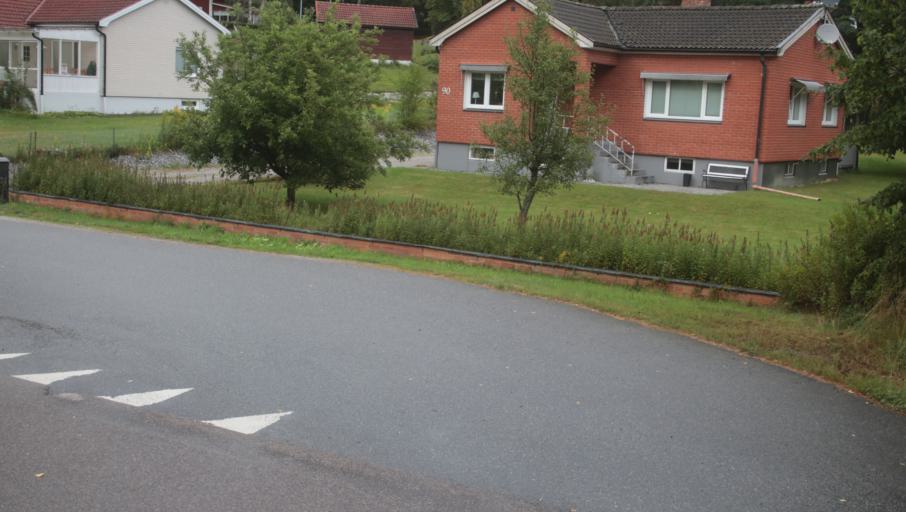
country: SE
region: Blekinge
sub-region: Karlshamns Kommun
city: Svangsta
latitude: 56.2679
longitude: 14.7673
